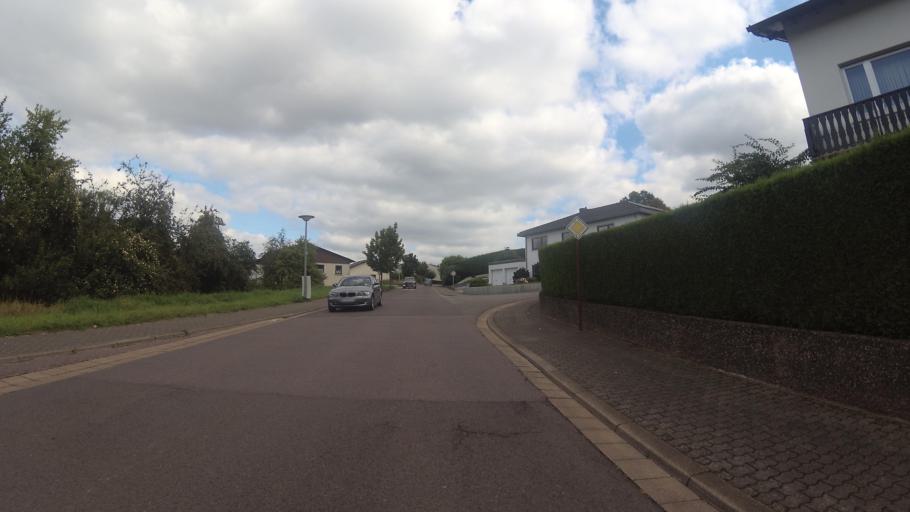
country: DE
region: Saarland
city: Wadgassen
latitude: 49.2548
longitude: 6.8017
